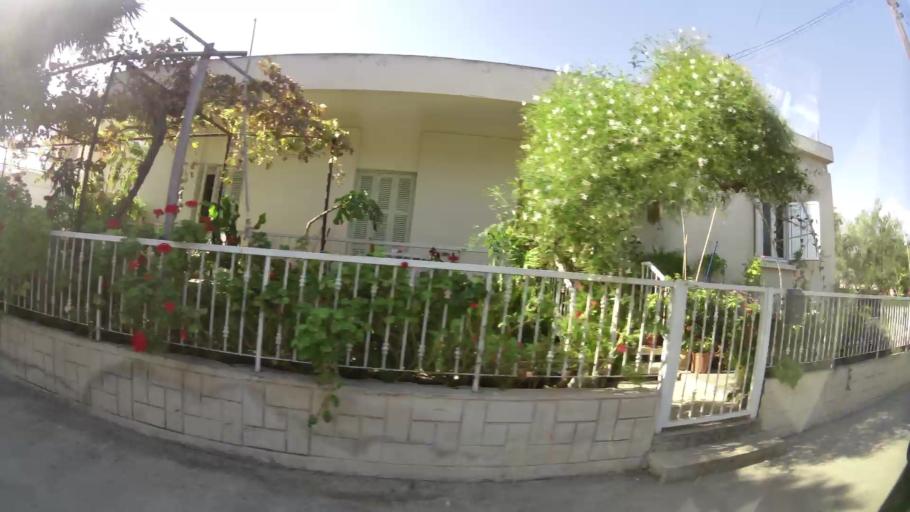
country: CY
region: Larnaka
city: Aradippou
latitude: 34.9523
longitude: 33.5839
